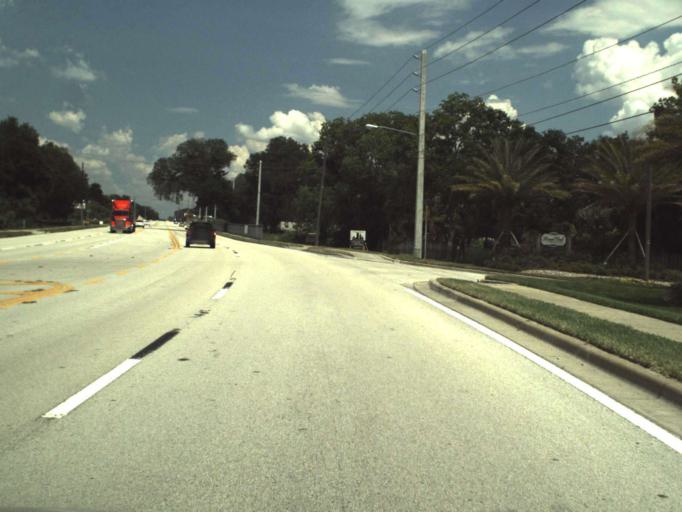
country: US
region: Florida
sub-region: Lake County
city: Leesburg
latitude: 28.8031
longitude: -81.9136
